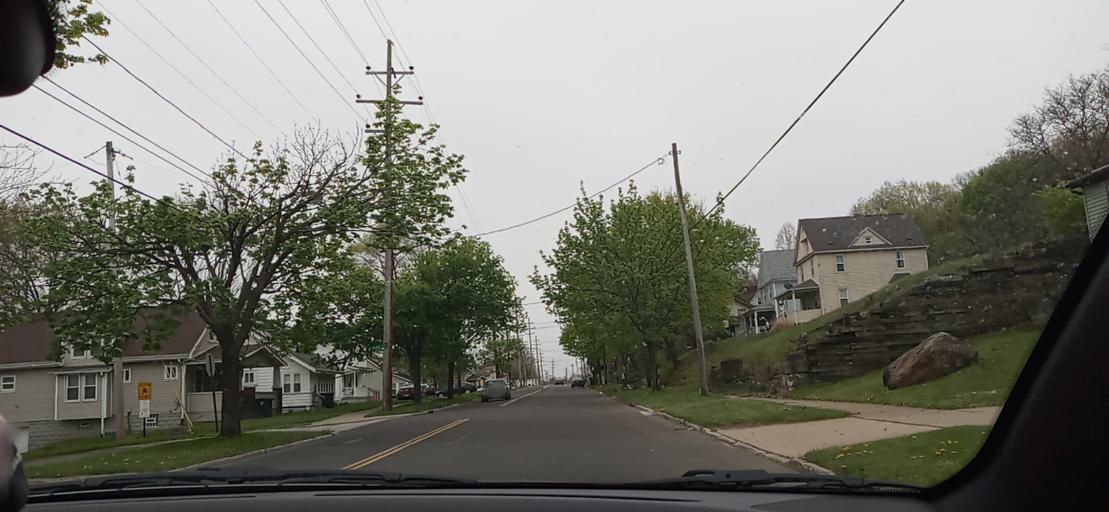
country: US
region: Ohio
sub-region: Summit County
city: Akron
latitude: 41.0514
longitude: -81.5483
